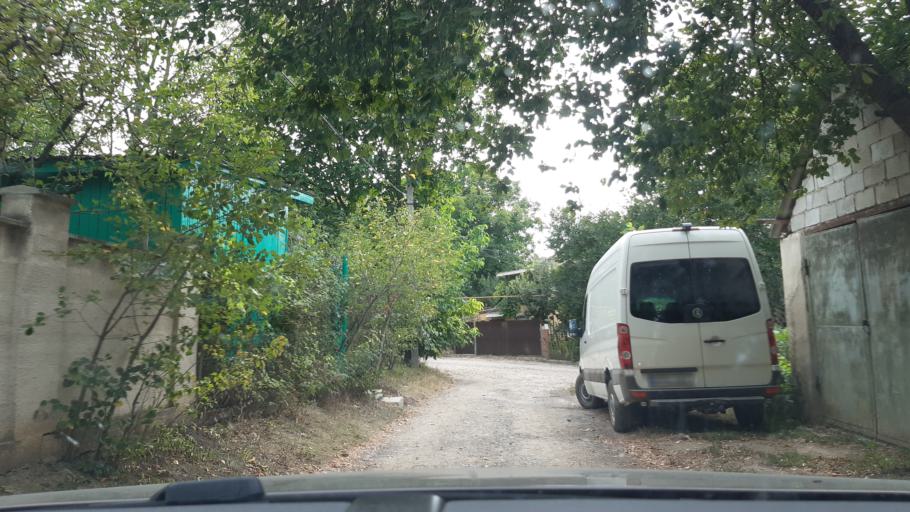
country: MD
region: Chisinau
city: Vatra
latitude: 47.0578
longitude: 28.7335
